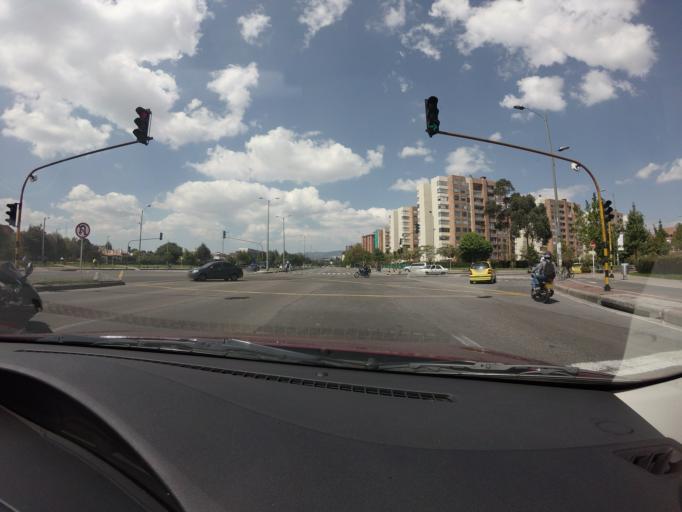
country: CO
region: Bogota D.C.
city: Barrio San Luis
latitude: 4.7259
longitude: -74.0712
